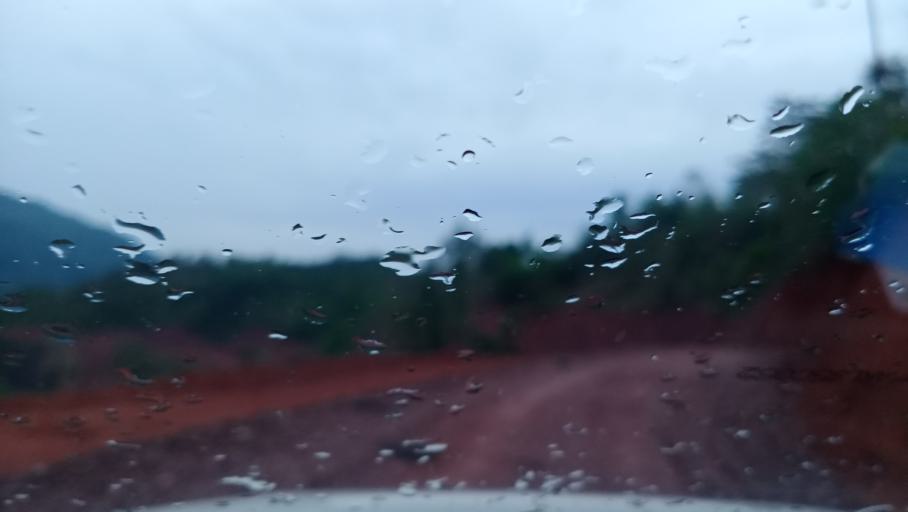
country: CN
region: Yunnan
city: Menglie
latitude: 22.2021
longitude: 101.6726
